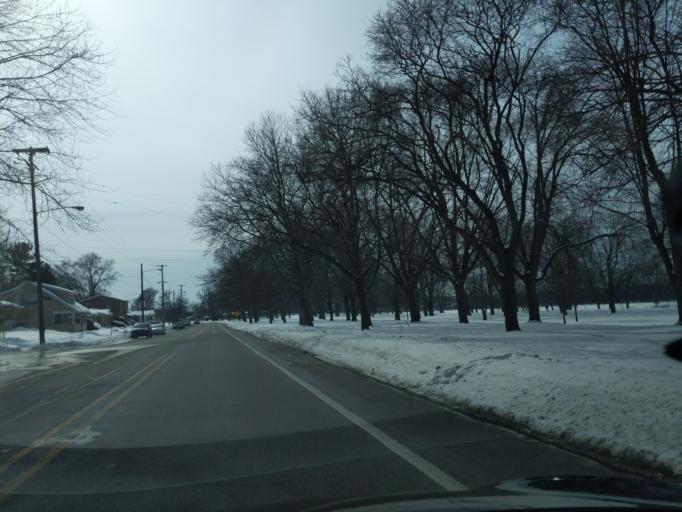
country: US
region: Michigan
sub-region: Kent County
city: Comstock Park
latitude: 43.0021
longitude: -85.6697
